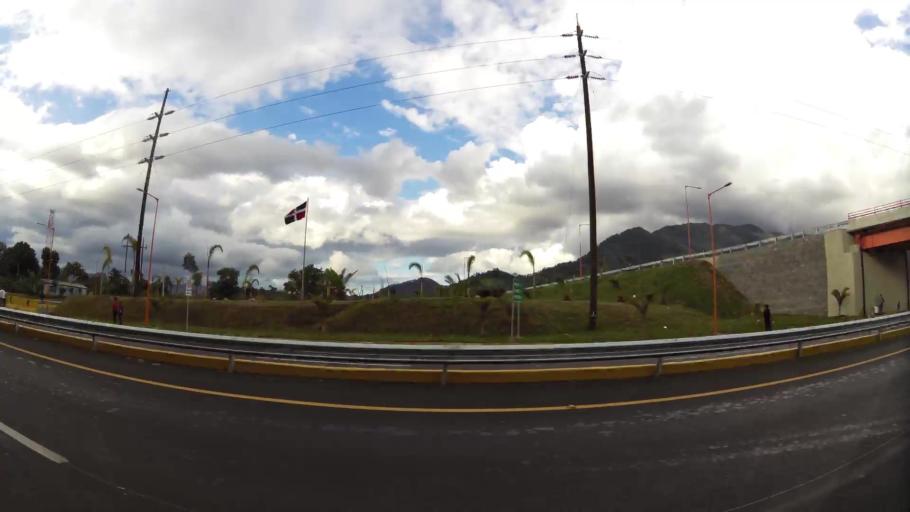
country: DO
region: Monsenor Nouel
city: Piedra Blanca
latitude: 18.8401
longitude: -70.3067
